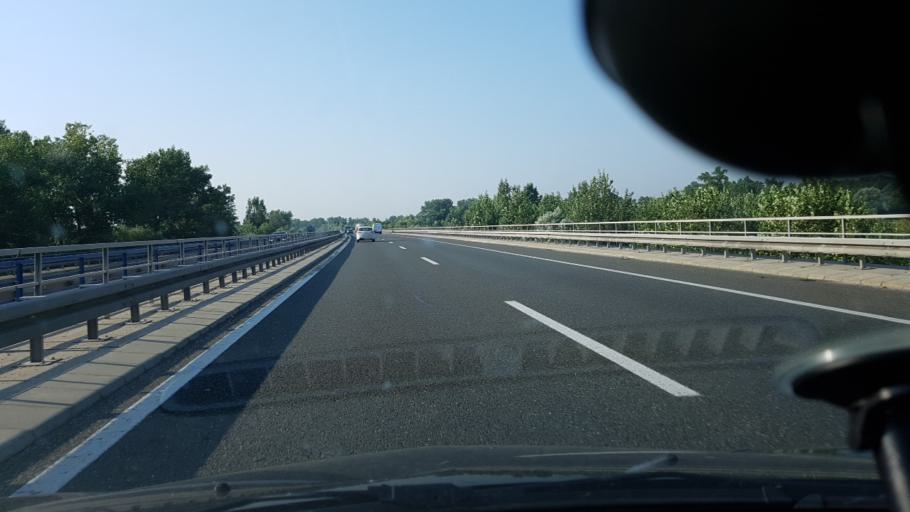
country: HR
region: Zagrebacka
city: Bestovje
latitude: 45.8334
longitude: 15.8188
